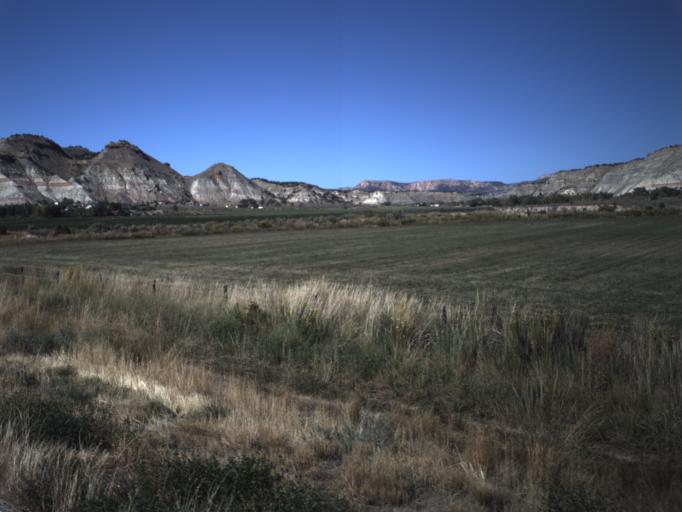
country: US
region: Utah
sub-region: Garfield County
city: Panguitch
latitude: 37.5668
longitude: -112.0498
